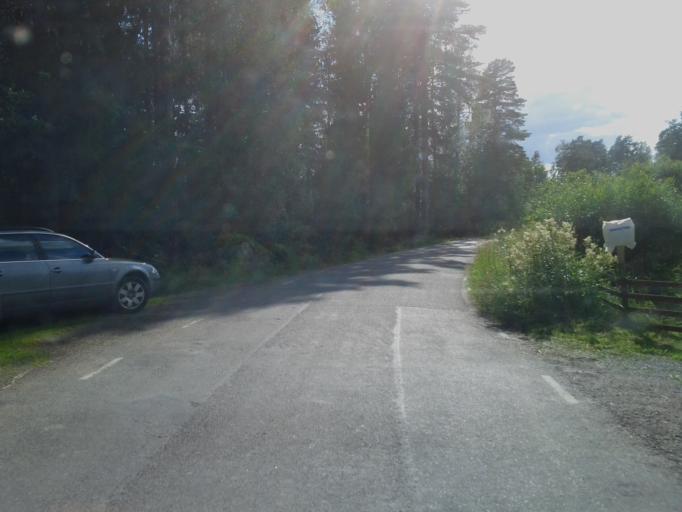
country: SE
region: Vaestmanland
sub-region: Sala Kommun
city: Sala
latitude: 59.9245
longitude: 16.4896
